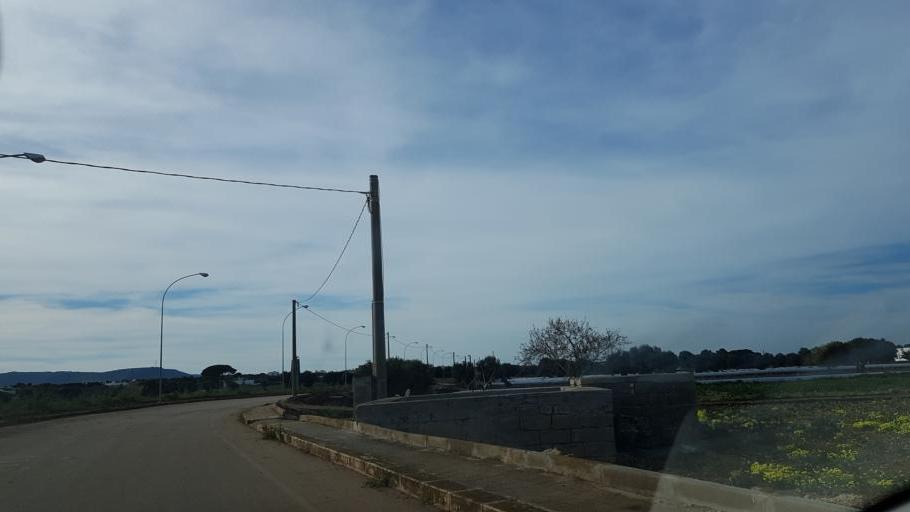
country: IT
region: Apulia
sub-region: Provincia di Brindisi
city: Fasano
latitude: 40.8935
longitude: 17.3648
